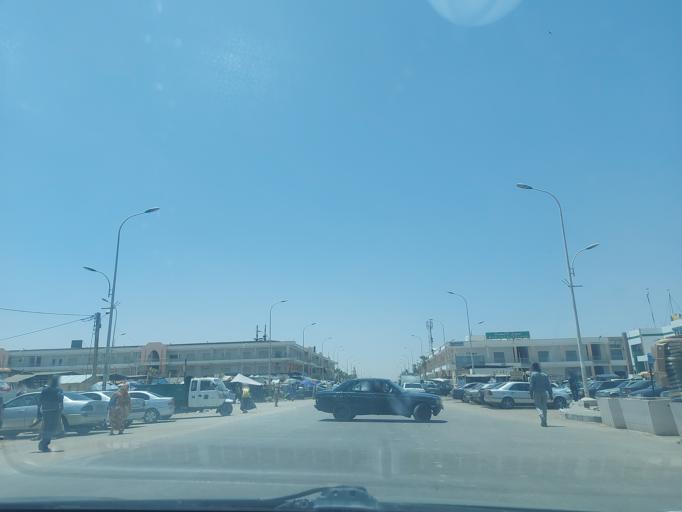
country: MR
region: Nouakchott
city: Nouakchott
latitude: 18.0864
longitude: -15.9806
